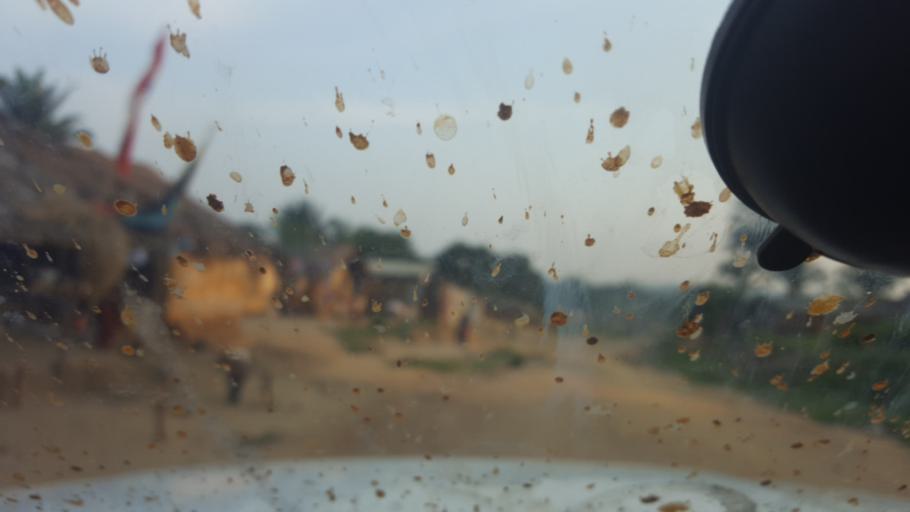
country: CD
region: Bandundu
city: Mushie
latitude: -3.7419
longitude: 16.6519
